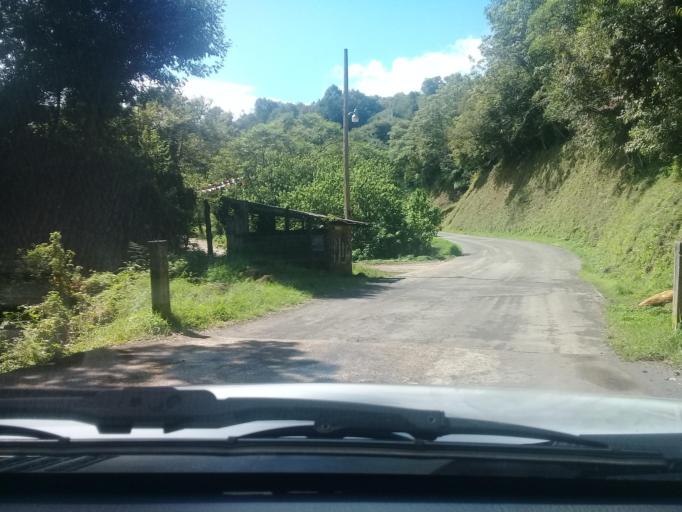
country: MX
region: Veracruz
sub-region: Tlalnelhuayocan
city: Otilpan
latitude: 19.5662
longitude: -96.9838
